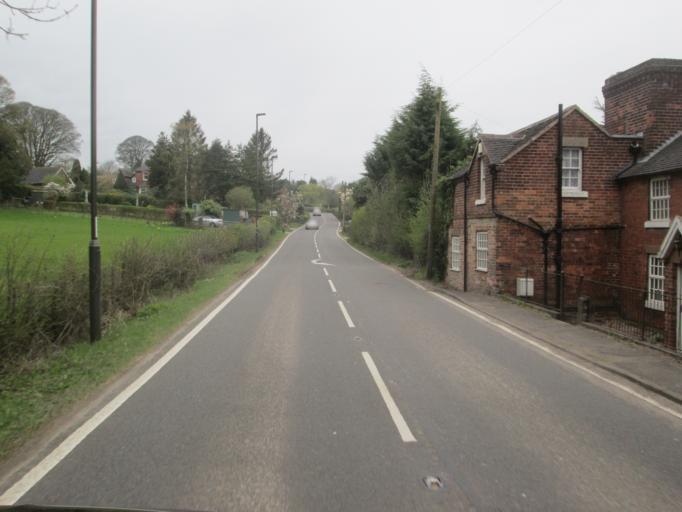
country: GB
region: England
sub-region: Derbyshire
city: Wirksworth
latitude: 53.0136
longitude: -1.5649
